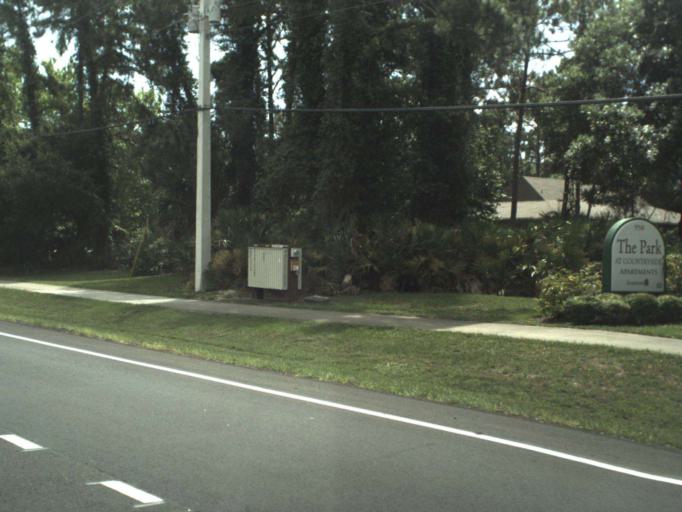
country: US
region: Florida
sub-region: Volusia County
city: Port Orange
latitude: 29.1228
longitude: -81.0130
